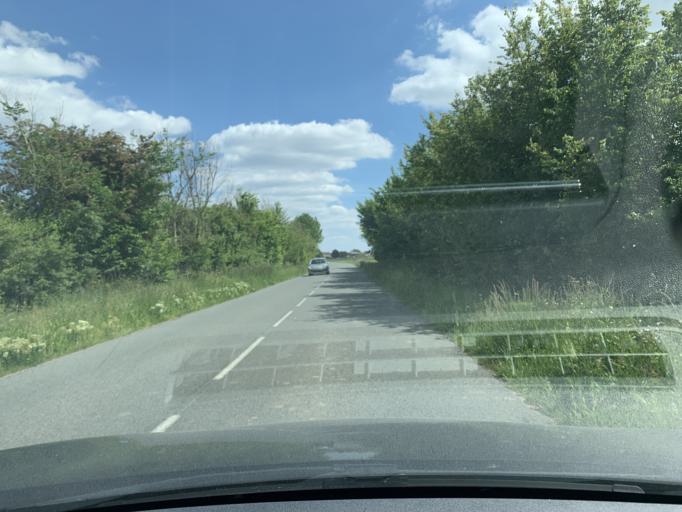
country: FR
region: Nord-Pas-de-Calais
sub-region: Departement du Pas-de-Calais
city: Oisy-le-Verger
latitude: 50.2586
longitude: 3.1059
